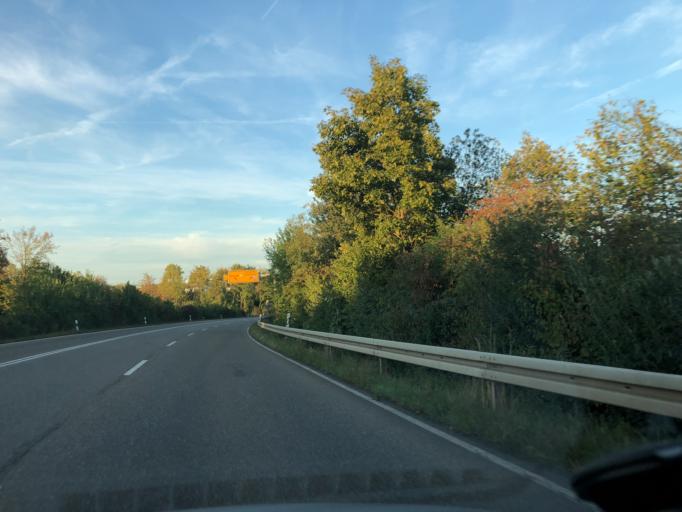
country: DE
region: Baden-Wuerttemberg
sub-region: Regierungsbezirk Stuttgart
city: Kornwestheim
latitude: 48.8460
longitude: 9.1814
